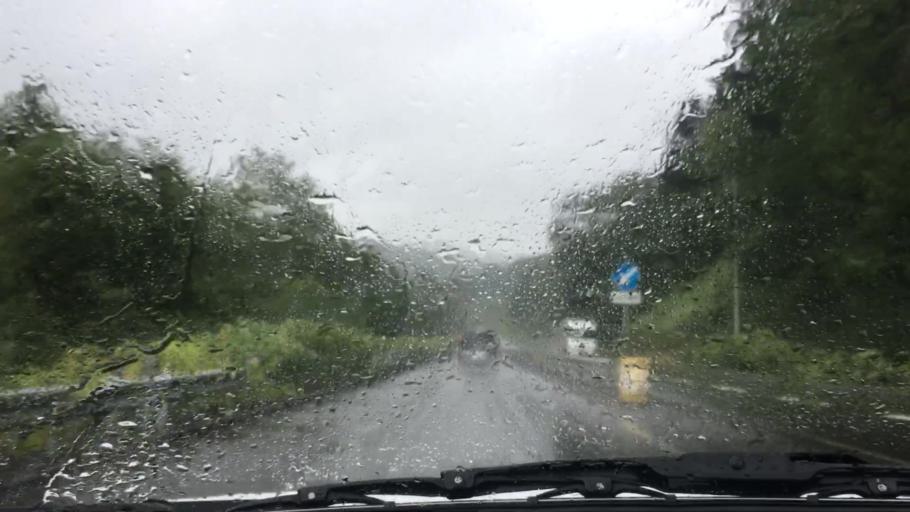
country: JP
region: Hokkaido
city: Otaru
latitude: 42.8483
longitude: 141.0486
